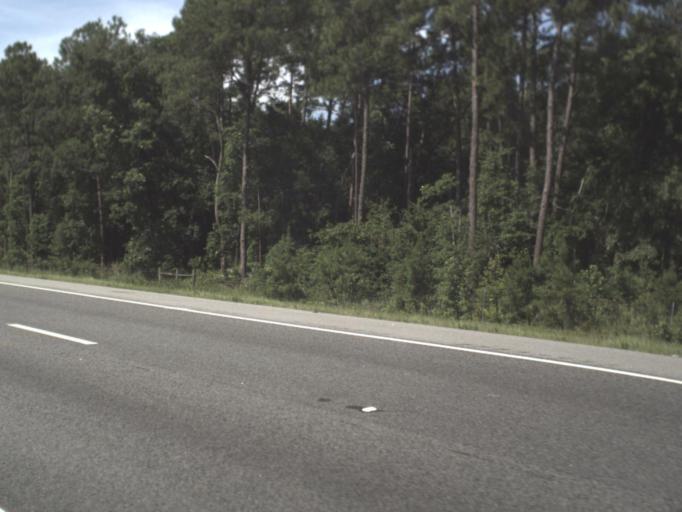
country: US
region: Florida
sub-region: Saint Johns County
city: Fruit Cove
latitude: 30.0733
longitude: -81.4989
